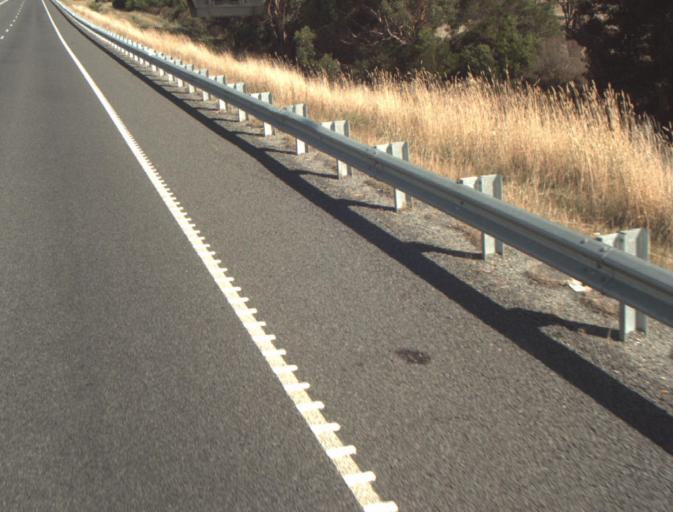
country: AU
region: Tasmania
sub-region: Launceston
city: Mayfield
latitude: -41.3635
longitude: 147.1076
